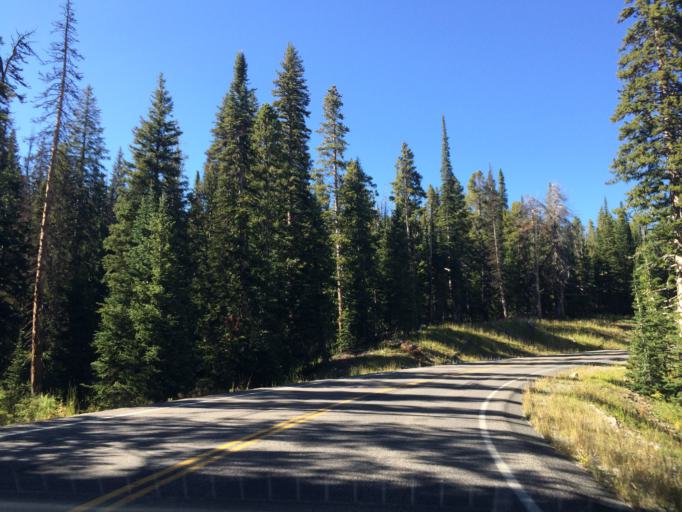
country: US
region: Montana
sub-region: Gallatin County
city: West Yellowstone
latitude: 44.7731
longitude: -110.4592
